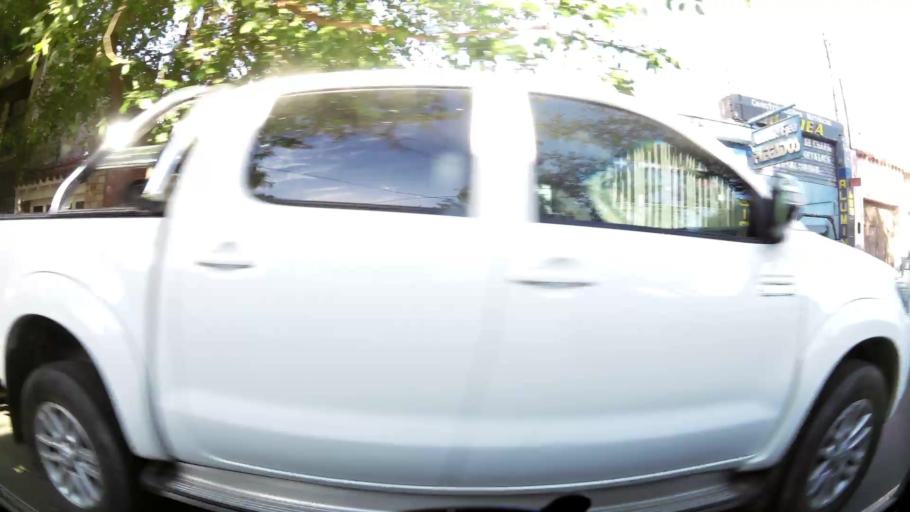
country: AR
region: Mendoza
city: Mendoza
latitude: -32.9012
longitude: -68.8351
